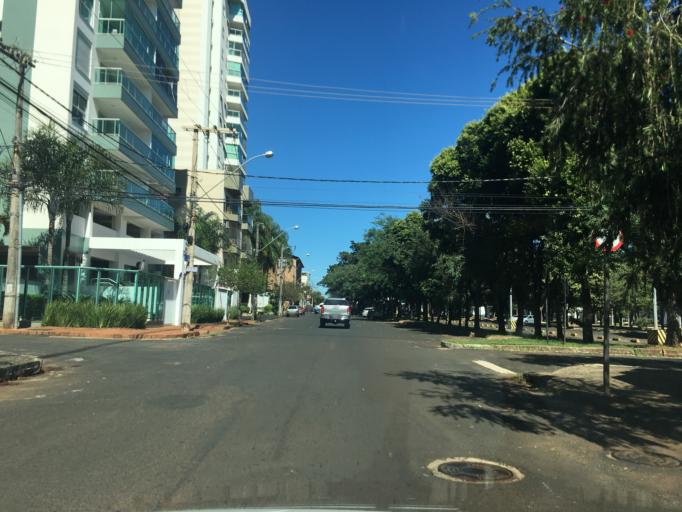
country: BR
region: Minas Gerais
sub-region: Uberlandia
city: Uberlandia
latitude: -18.9322
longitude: -48.2906
